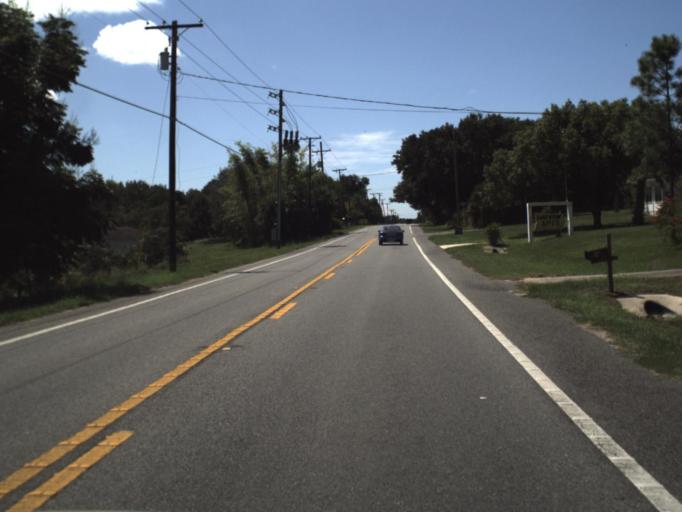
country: US
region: Florida
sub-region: Polk County
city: Lake Wales
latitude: 27.9543
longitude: -81.5947
